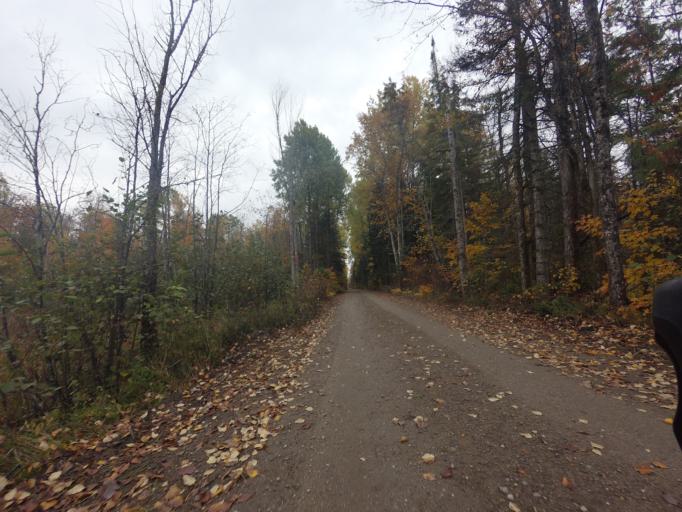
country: CA
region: Ontario
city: Renfrew
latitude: 45.1796
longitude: -76.6836
